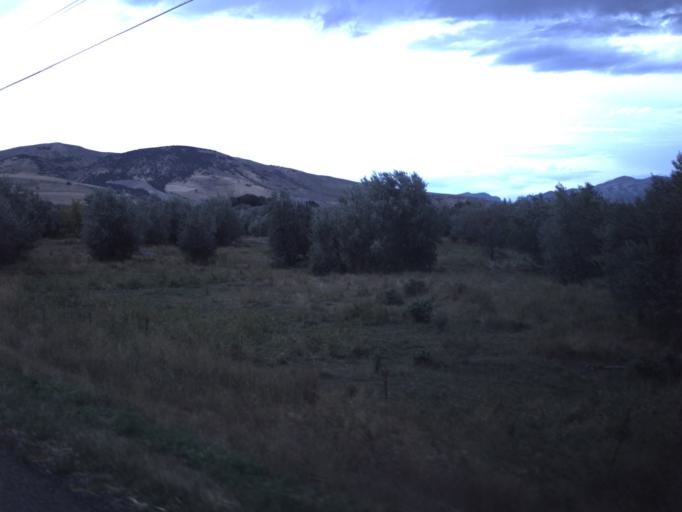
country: US
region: Utah
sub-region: Cache County
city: Lewiston
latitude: 41.9754
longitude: -111.9352
